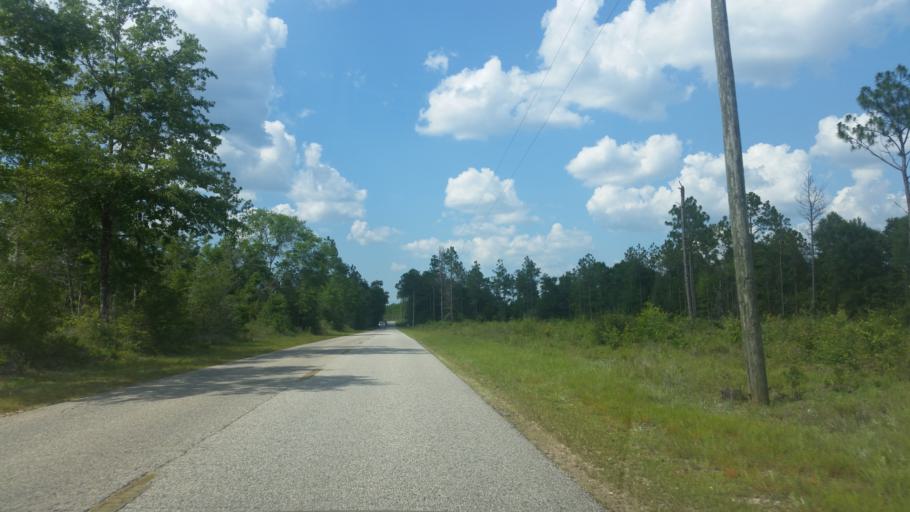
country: US
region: Florida
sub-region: Santa Rosa County
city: East Milton
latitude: 30.6687
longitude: -86.8777
